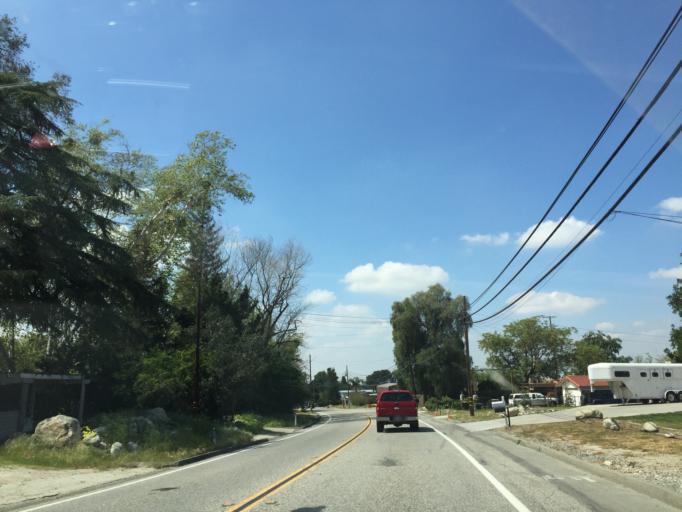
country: US
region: California
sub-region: San Bernardino County
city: Yucaipa
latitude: 34.0737
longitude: -117.0776
